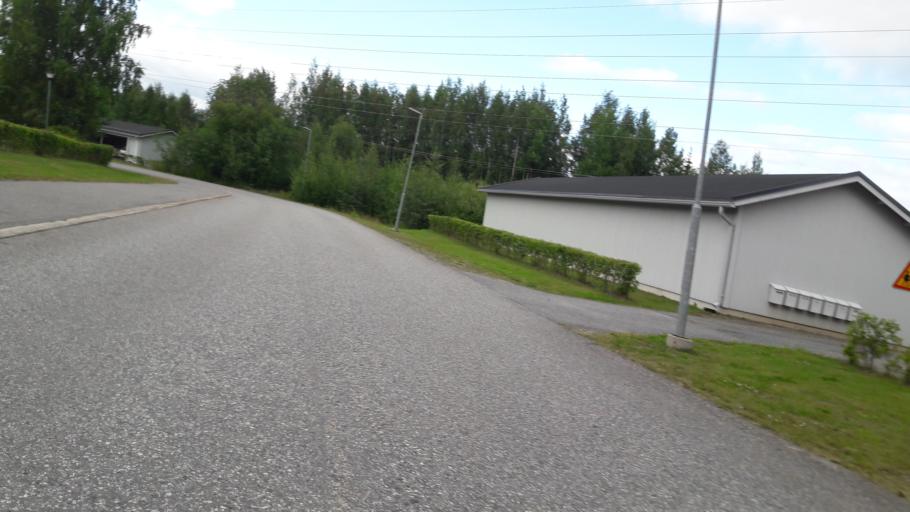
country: FI
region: North Karelia
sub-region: Joensuu
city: Joensuu
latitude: 62.5916
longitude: 29.8041
